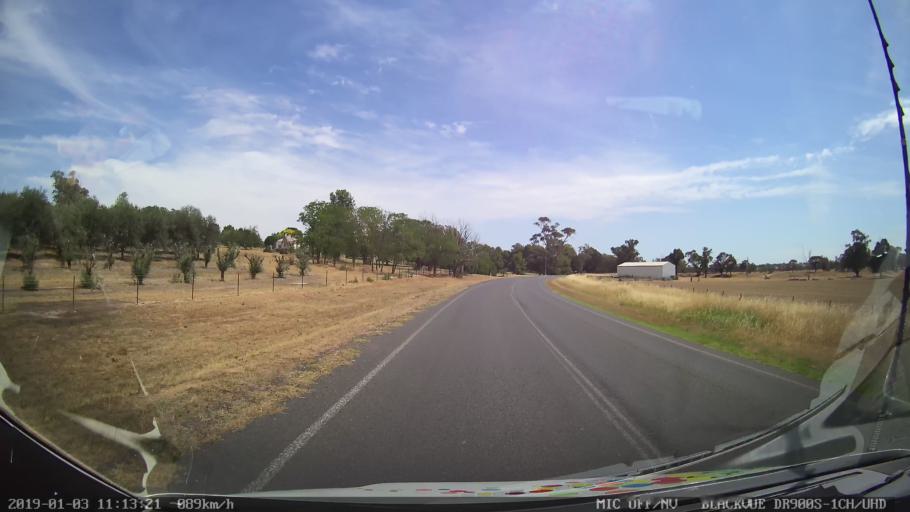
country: AU
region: New South Wales
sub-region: Young
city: Young
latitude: -34.1897
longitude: 148.2606
